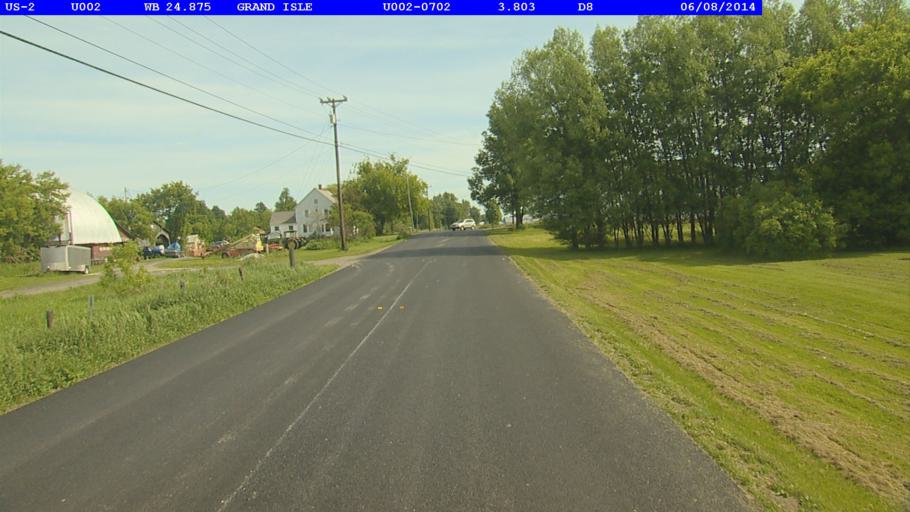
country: US
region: Vermont
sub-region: Grand Isle County
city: North Hero
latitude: 44.7134
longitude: -73.2981
